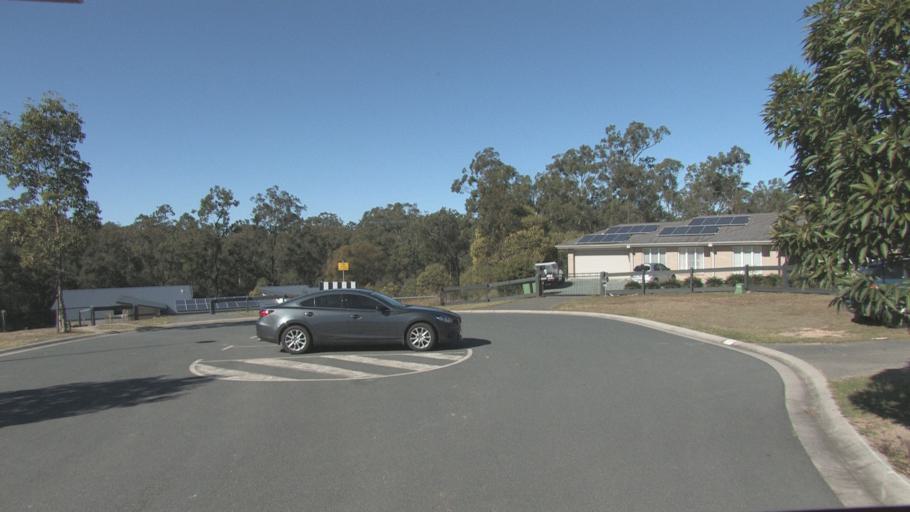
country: AU
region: Queensland
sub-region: Ipswich
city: Springfield Lakes
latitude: -27.7254
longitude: 152.9141
